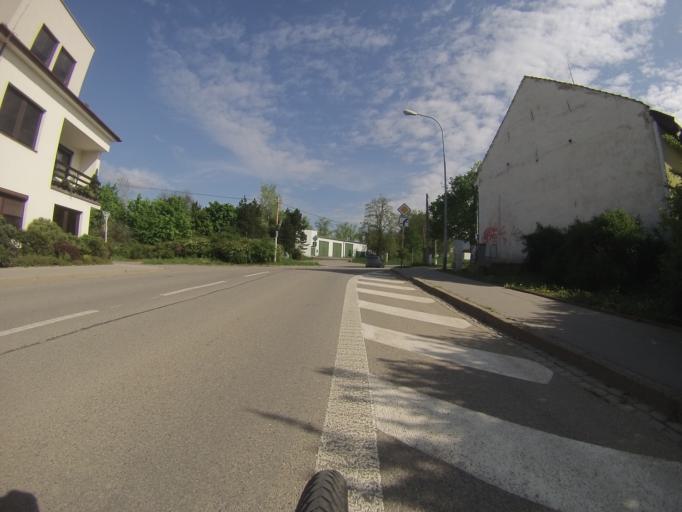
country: CZ
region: South Moravian
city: Troubsko
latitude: 49.2245
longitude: 16.5187
